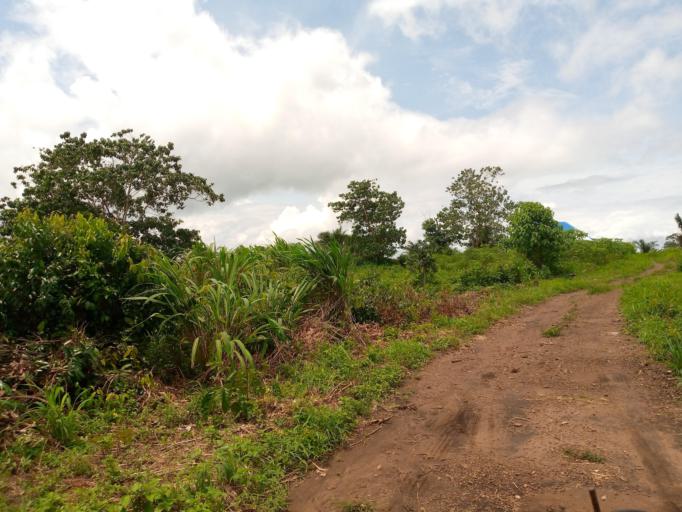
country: SL
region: Northern Province
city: Magburaka
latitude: 8.7308
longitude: -11.9291
